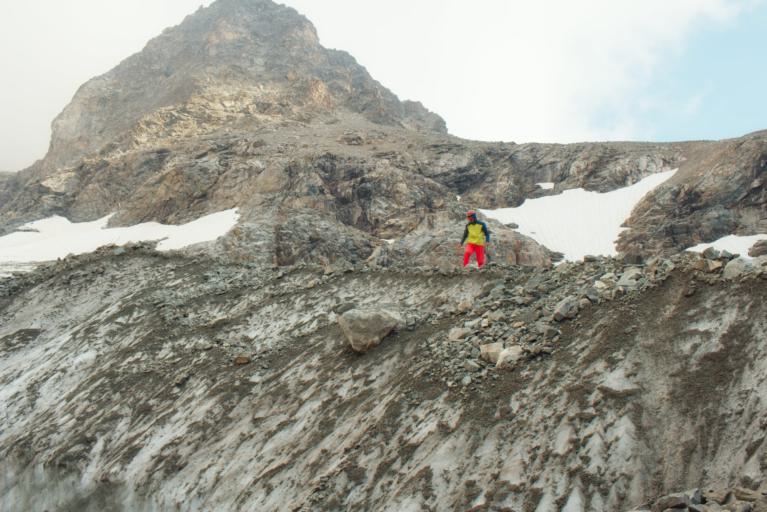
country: RU
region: Karachayevo-Cherkesiya
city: Nizhniy Arkhyz
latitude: 43.4266
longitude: 41.2556
